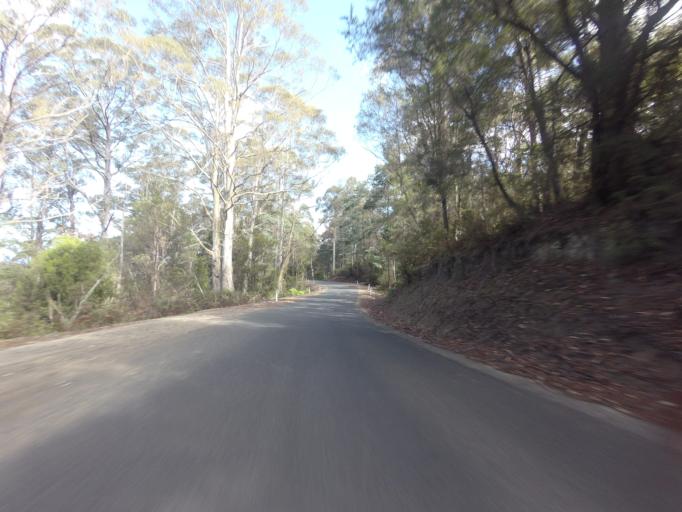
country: AU
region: Tasmania
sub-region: Break O'Day
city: St Helens
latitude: -41.6543
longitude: 148.2462
